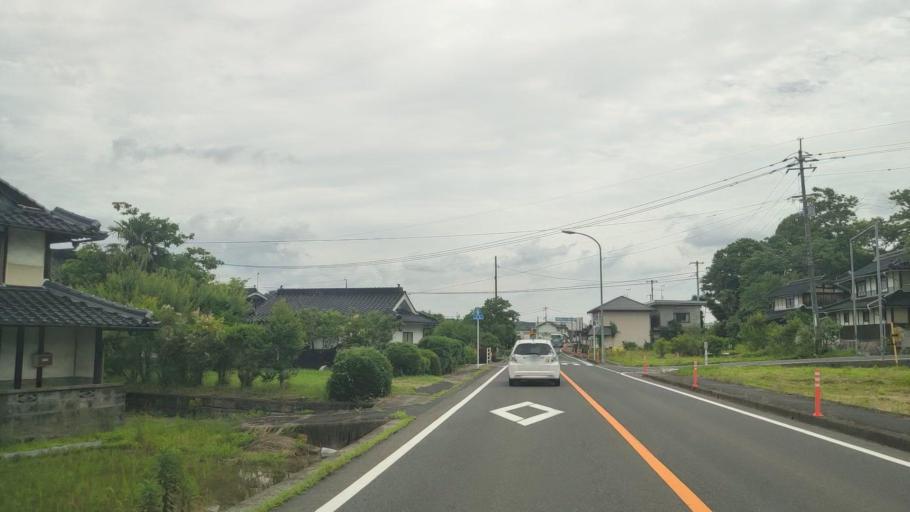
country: JP
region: Okayama
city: Tsuyama
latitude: 35.0592
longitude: 133.8907
